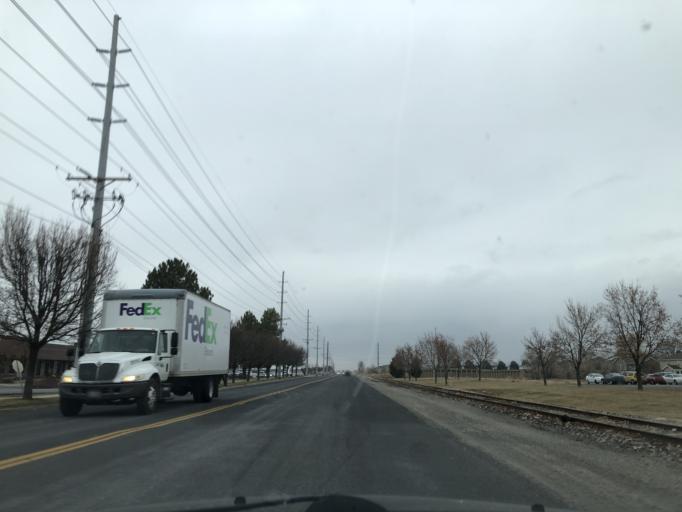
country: US
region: Utah
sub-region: Cache County
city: Logan
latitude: 41.7470
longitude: -111.8494
